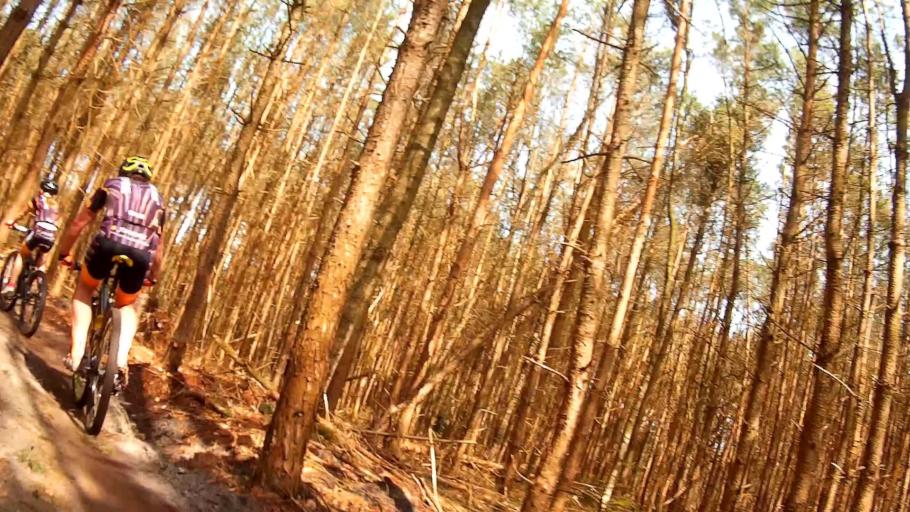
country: NL
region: North Holland
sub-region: Gemeente Hilversum
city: Hilversum
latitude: 52.1920
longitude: 5.2149
